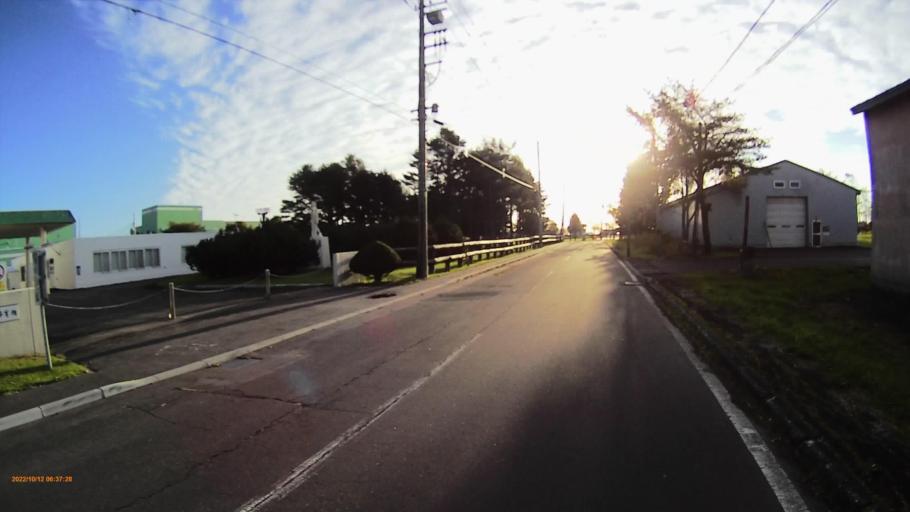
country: JP
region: Hokkaido
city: Kushiro
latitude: 42.8921
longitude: 143.9375
